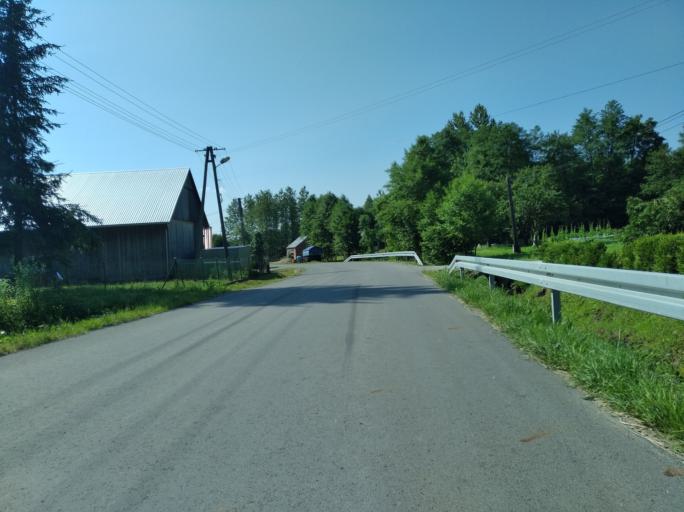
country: PL
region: Subcarpathian Voivodeship
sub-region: Powiat brzozowski
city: Nozdrzec
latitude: 49.8232
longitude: 22.1631
